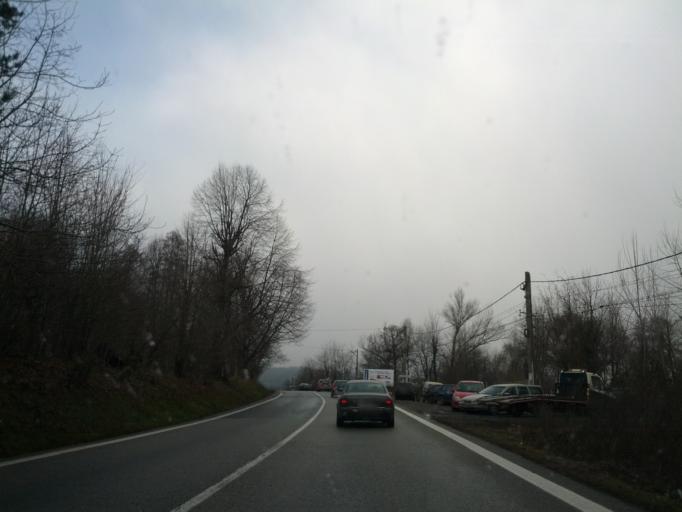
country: RO
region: Valcea
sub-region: Oras Calimanesti
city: Jiblea Veche
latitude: 45.2152
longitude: 24.3559
